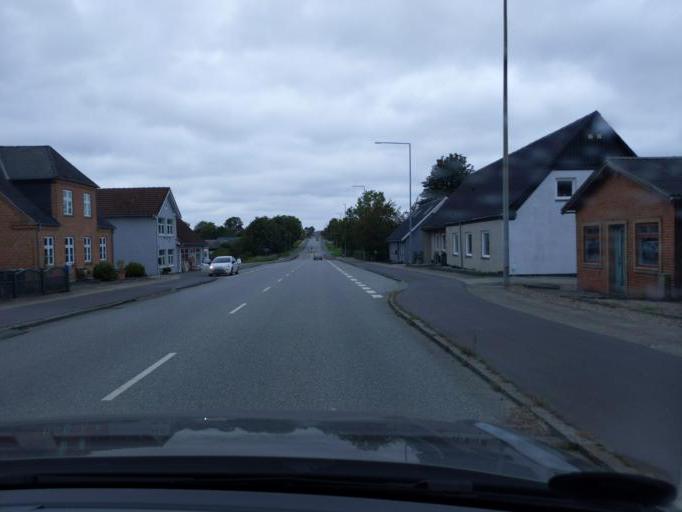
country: DK
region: Central Jutland
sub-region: Randers Kommune
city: Spentrup
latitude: 56.5146
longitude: 9.9469
